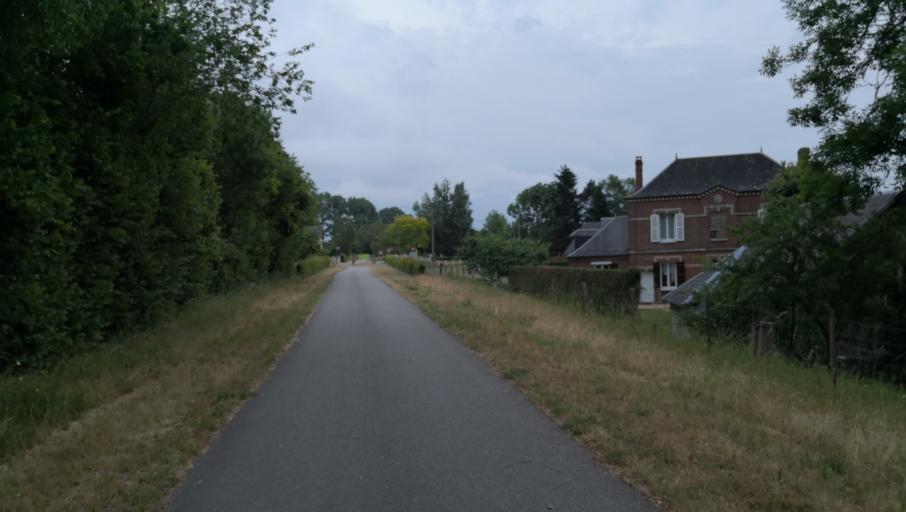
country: FR
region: Haute-Normandie
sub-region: Departement de la Seine-Maritime
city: Serqueux
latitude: 49.6475
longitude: 1.5249
